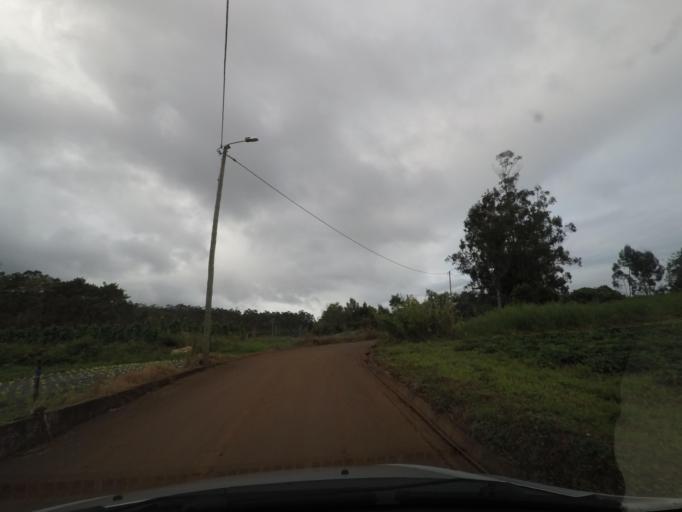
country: PT
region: Madeira
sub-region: Santana
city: Santana
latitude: 32.7807
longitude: -16.8778
